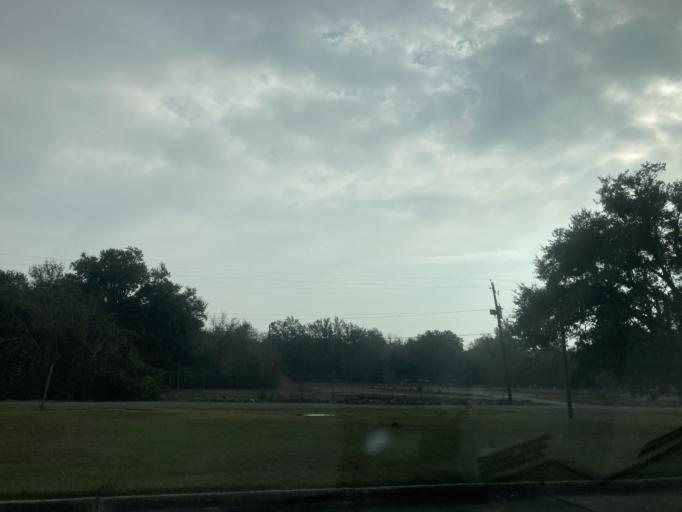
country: US
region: Mississippi
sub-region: Harrison County
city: Gulfport
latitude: 30.3709
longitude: -89.1154
